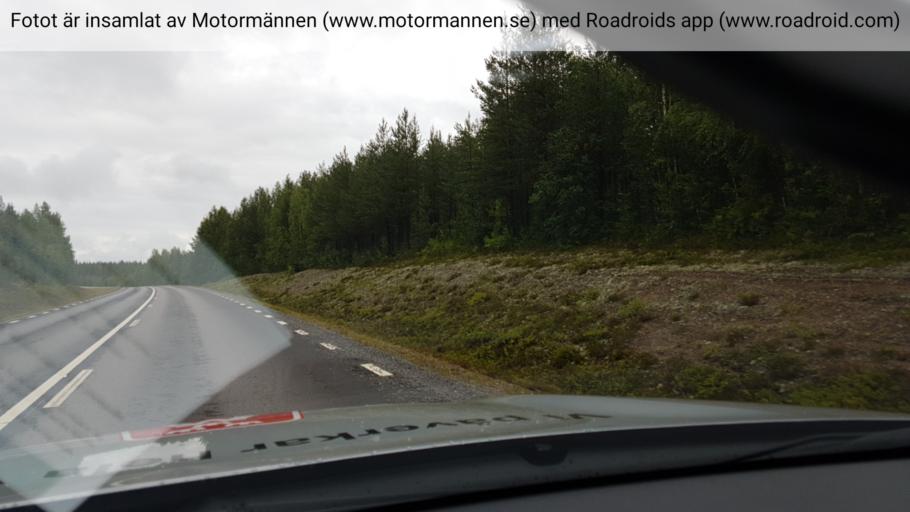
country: SE
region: Norrbotten
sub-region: Alvsbyns Kommun
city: AElvsbyn
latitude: 66.3660
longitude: 20.7257
